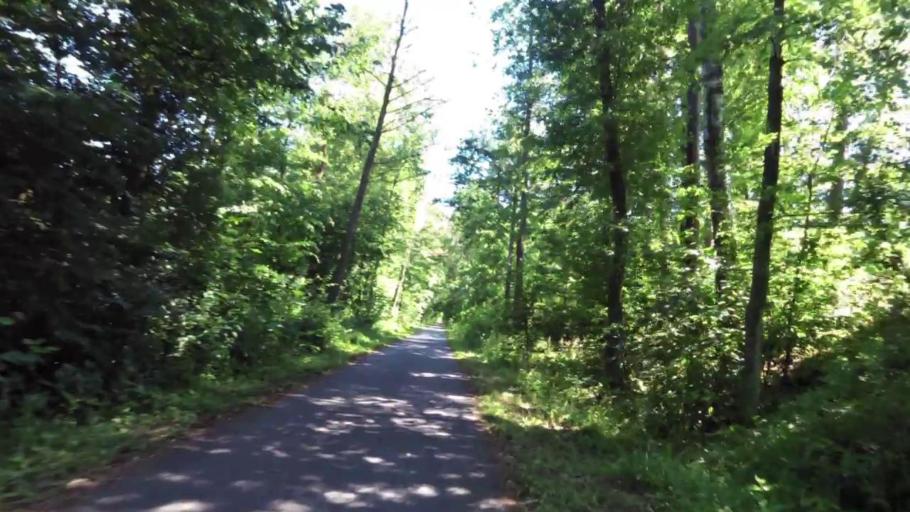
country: PL
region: West Pomeranian Voivodeship
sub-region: Powiat bialogardzki
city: Karlino
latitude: 54.0539
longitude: 15.8755
